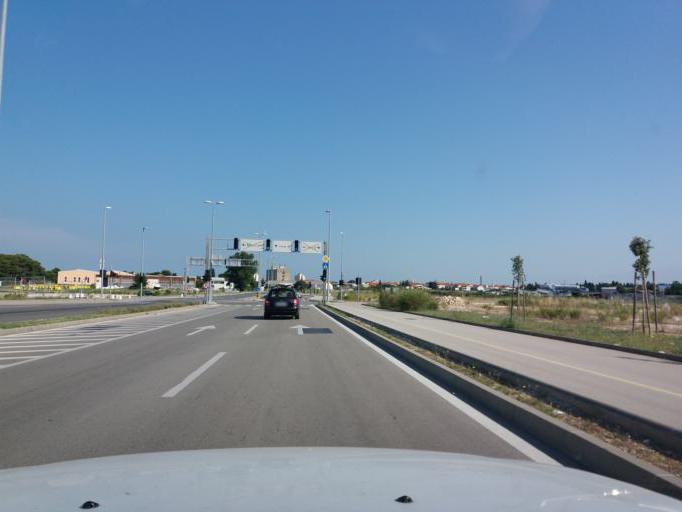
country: HR
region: Zadarska
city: Zadar
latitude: 44.0961
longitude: 15.2586
